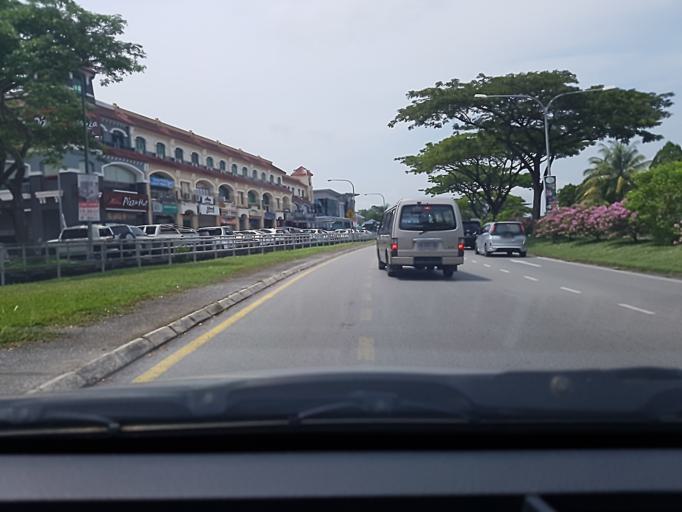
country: MY
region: Sarawak
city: Kuching
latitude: 1.5175
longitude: 110.3657
